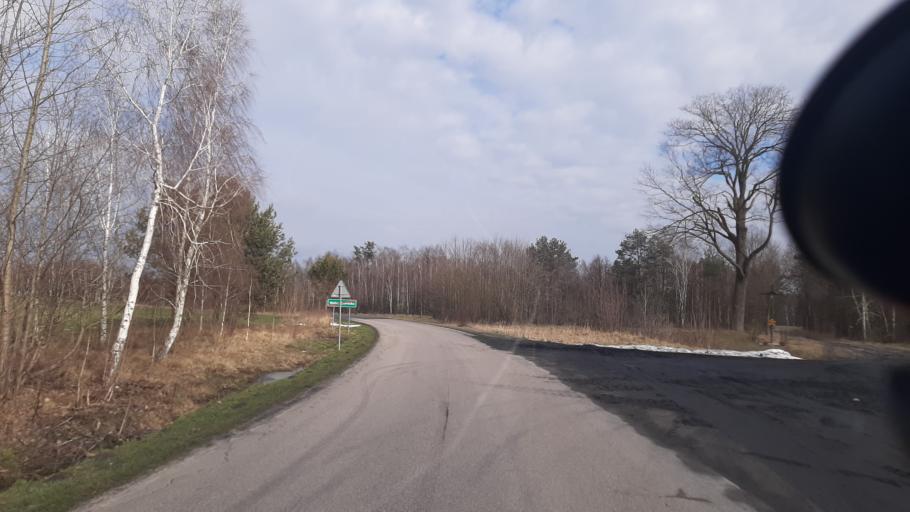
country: PL
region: Lublin Voivodeship
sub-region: Powiat lubartowski
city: Wola Sernicka
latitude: 51.4689
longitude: 22.7442
